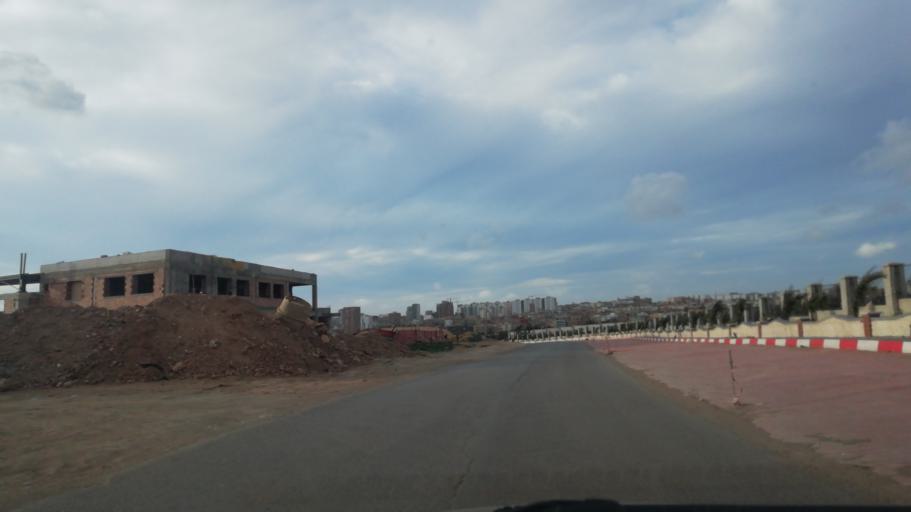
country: DZ
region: Oran
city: Bir el Djir
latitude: 35.7153
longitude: -0.5577
